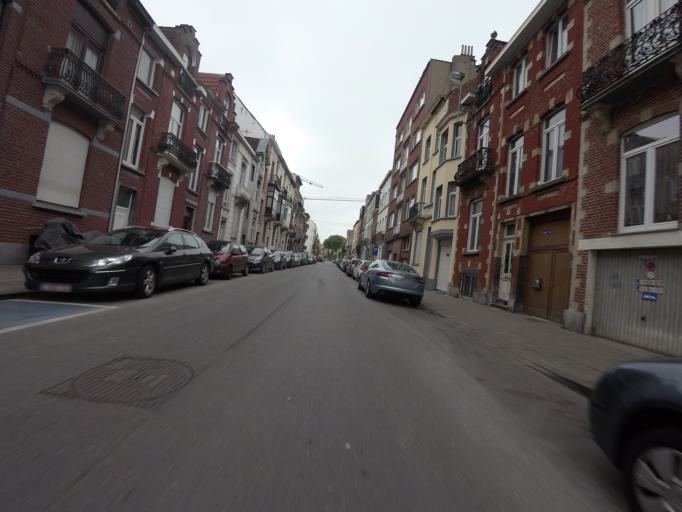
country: BE
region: Brussels Capital
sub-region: Bruxelles-Capitale
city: Brussels
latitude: 50.8731
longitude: 4.3549
